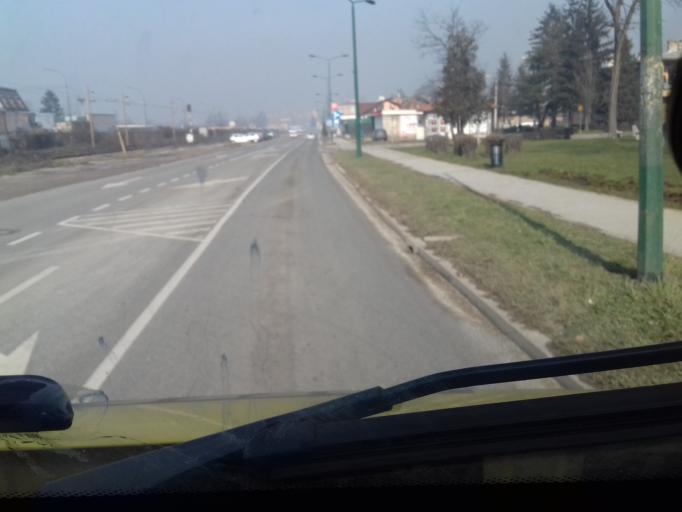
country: BA
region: Federation of Bosnia and Herzegovina
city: Ilijas
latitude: 43.9565
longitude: 18.2644
